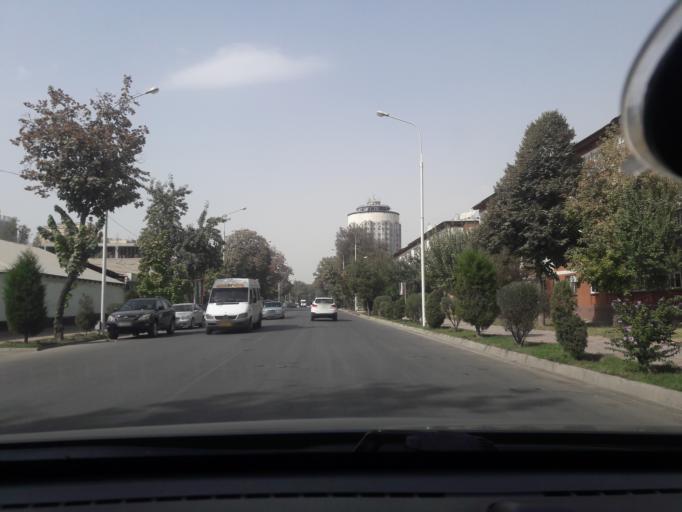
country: TJ
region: Dushanbe
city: Dushanbe
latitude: 38.5641
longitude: 68.7579
